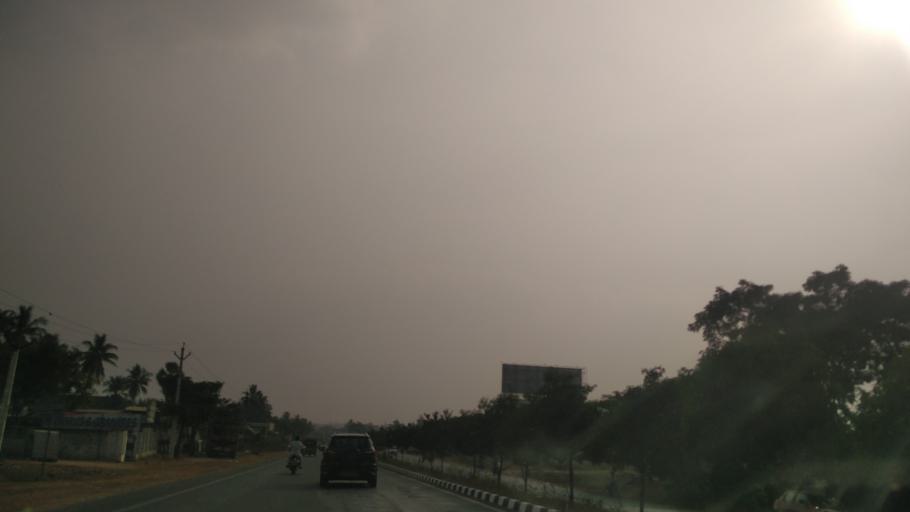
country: IN
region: Andhra Pradesh
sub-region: East Godavari
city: Rajahmundry
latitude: 16.9889
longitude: 81.7995
